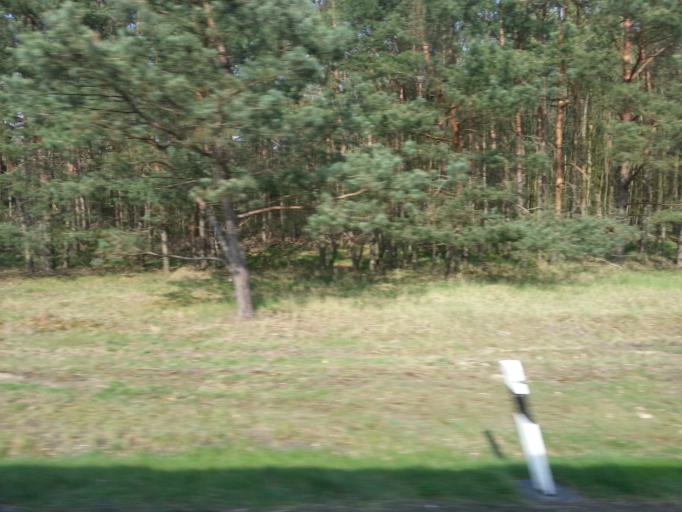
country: DE
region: Brandenburg
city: Fehrbellin
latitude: 52.7627
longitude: 12.8282
